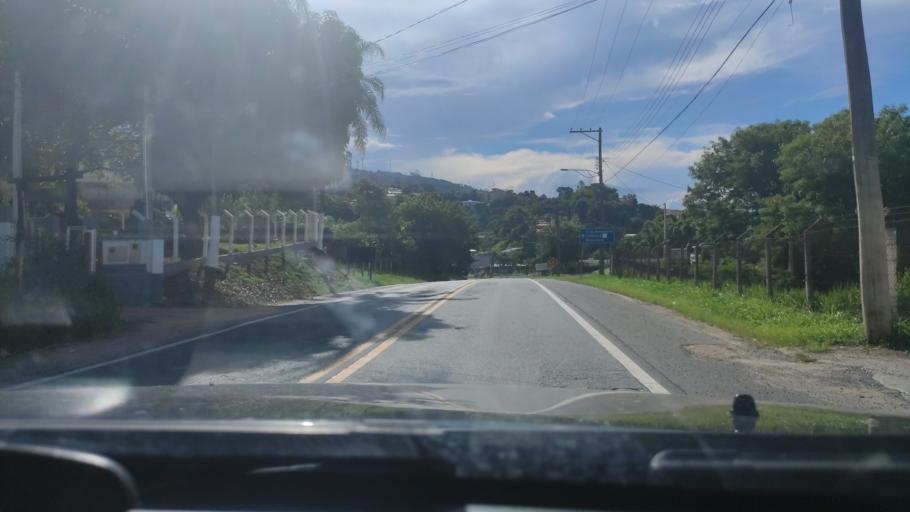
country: BR
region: Sao Paulo
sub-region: Aguas De Lindoia
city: Aguas de Lindoia
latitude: -22.5274
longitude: -46.6430
